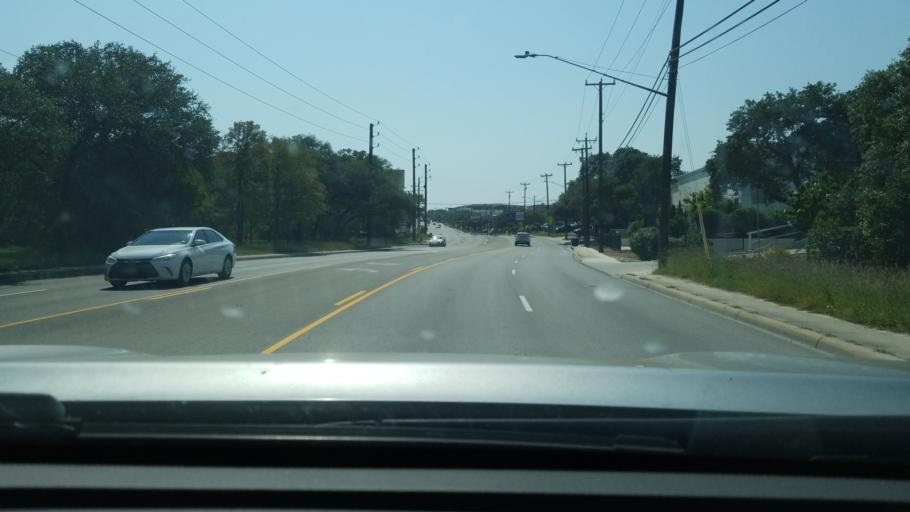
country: US
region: Texas
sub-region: Bexar County
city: Shavano Park
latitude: 29.5544
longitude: -98.5685
